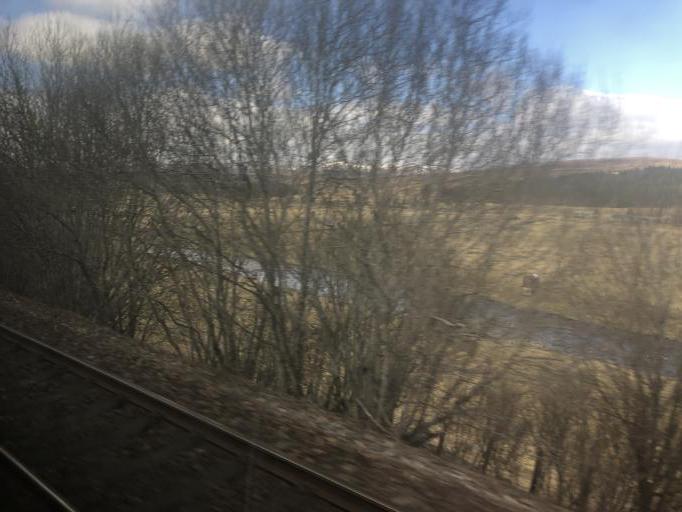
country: GB
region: Scotland
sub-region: Perth and Kinross
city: Aberfeldy
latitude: 56.7983
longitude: -4.0509
